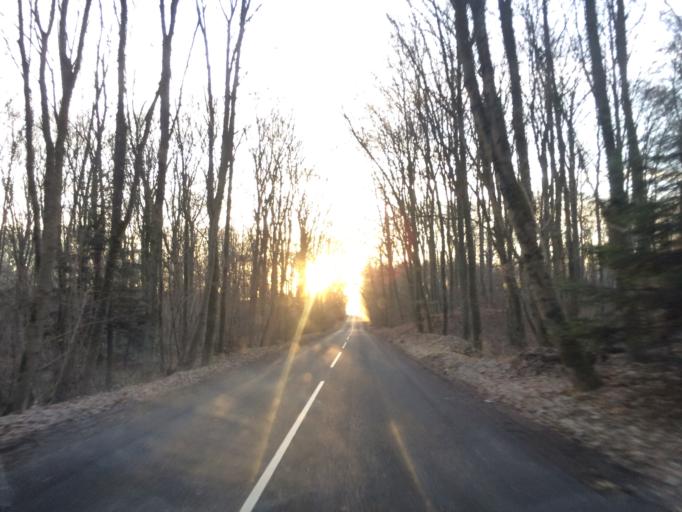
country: DK
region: South Denmark
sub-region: Odense Kommune
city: Bellinge
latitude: 55.2888
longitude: 10.2902
